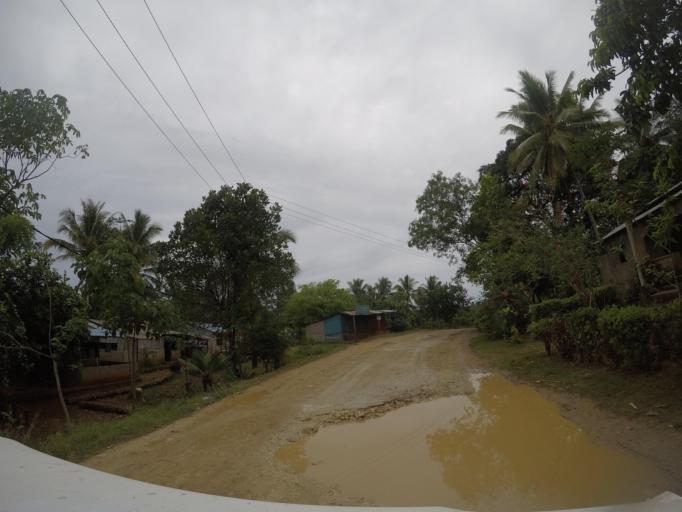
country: TL
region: Lautem
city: Lospalos
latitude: -8.5372
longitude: 126.9967
